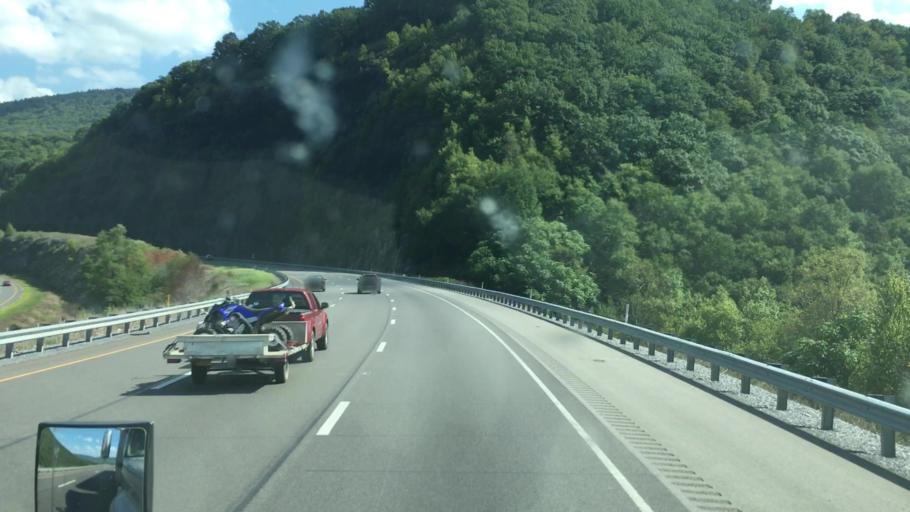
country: US
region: Pennsylvania
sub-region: Clinton County
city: Castanea
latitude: 41.0625
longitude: -77.3965
